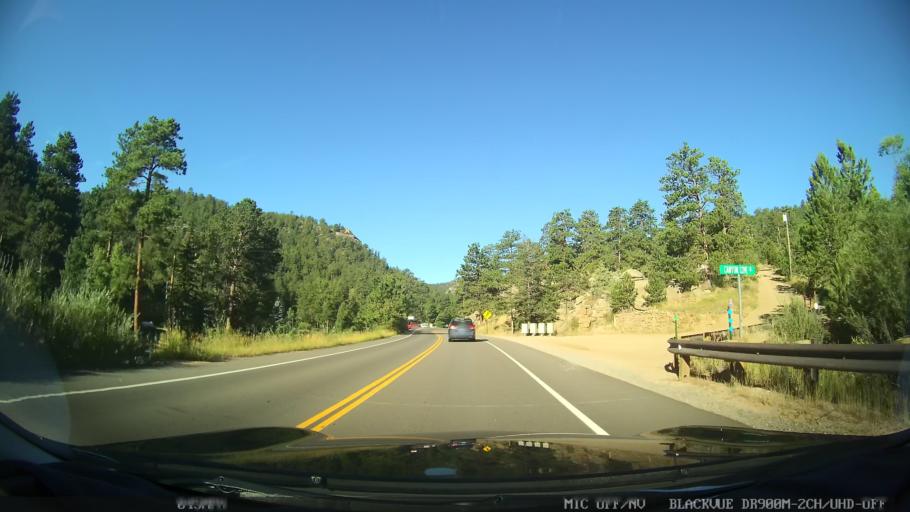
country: US
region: Colorado
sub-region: Larimer County
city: Estes Park
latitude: 40.3910
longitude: -105.4557
